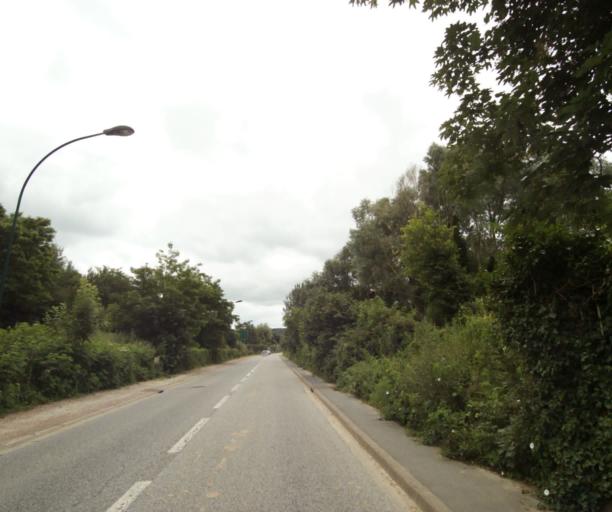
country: FR
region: Ile-de-France
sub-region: Departement des Yvelines
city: Saint-Cyr-l'Ecole
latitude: 48.8115
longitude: 2.0778
